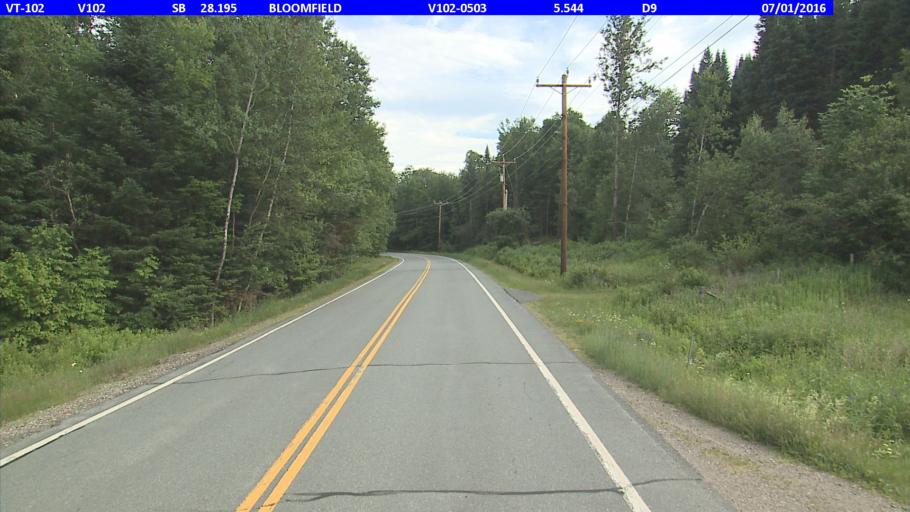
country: US
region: New Hampshire
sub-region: Coos County
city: Colebrook
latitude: 44.8101
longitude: -71.5755
